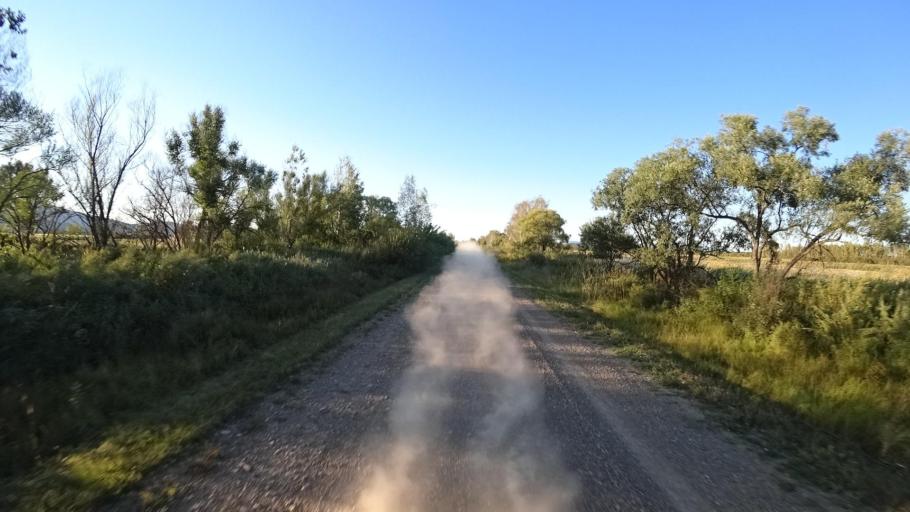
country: RU
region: Primorskiy
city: Kirovskiy
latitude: 44.7984
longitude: 133.6215
